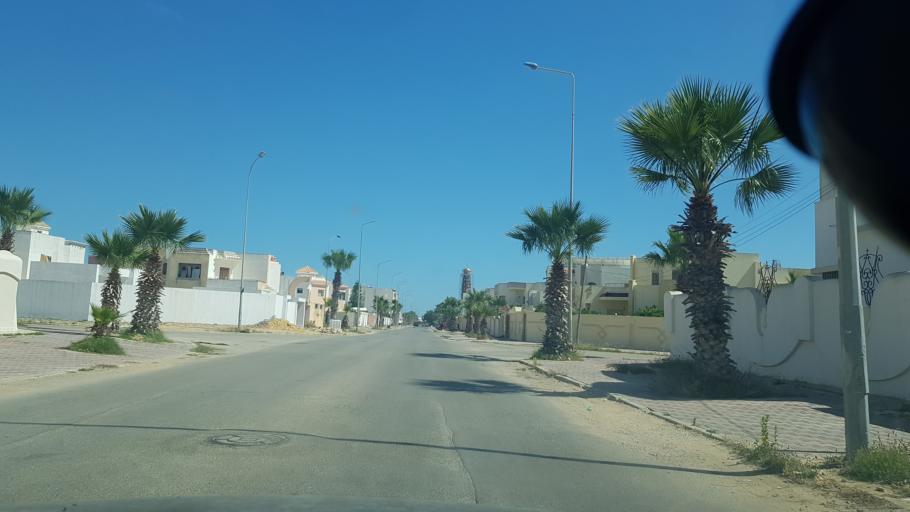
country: TN
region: Safaqis
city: Al Qarmadah
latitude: 34.8304
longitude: 10.7568
